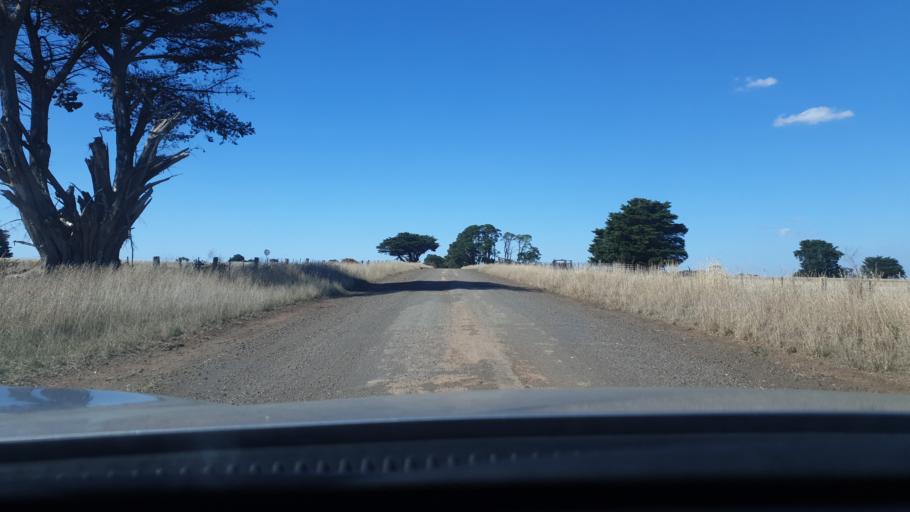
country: AU
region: Victoria
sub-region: Warrnambool
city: Warrnambool
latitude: -38.1649
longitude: 142.3837
